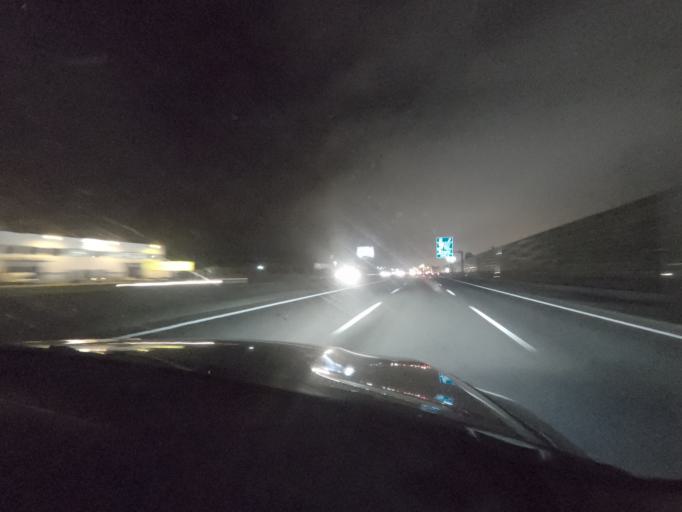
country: PT
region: Lisbon
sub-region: Vila Franca de Xira
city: Castanheira do Ribatejo
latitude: 38.9851
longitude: -8.9721
